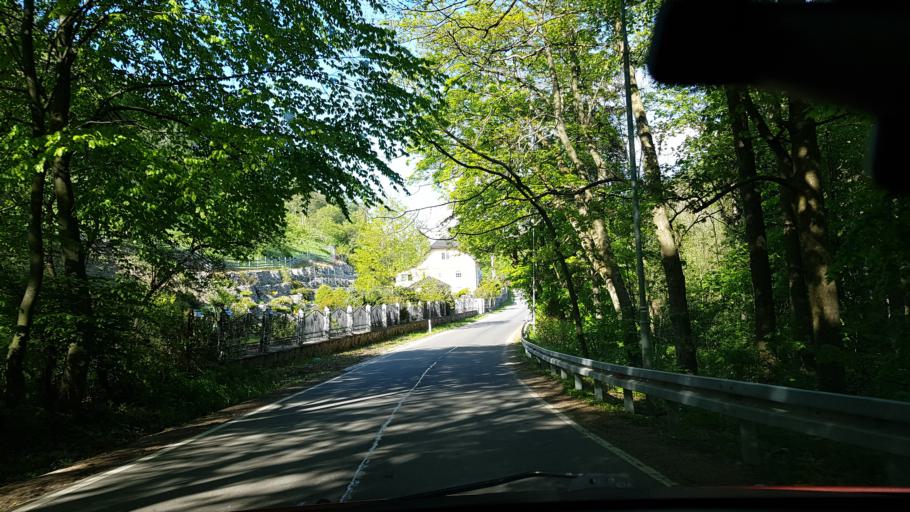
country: PL
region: Lower Silesian Voivodeship
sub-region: Powiat zabkowicki
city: Budzow
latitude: 50.5704
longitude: 16.6445
